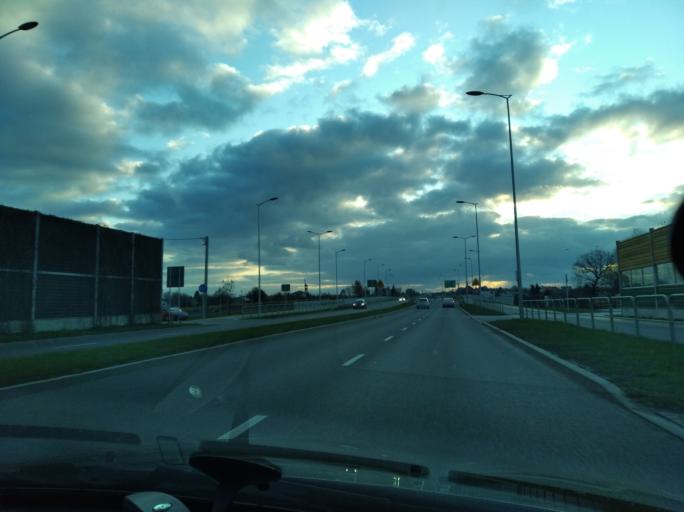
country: PL
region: Subcarpathian Voivodeship
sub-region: Powiat rzeszowski
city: Boguchwala
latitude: 50.0112
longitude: 21.9670
